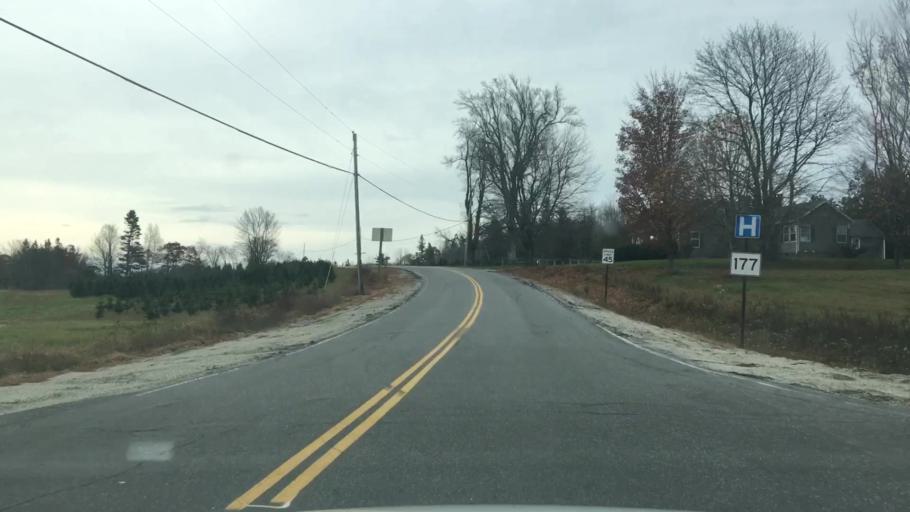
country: US
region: Maine
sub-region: Hancock County
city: Penobscot
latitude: 44.4429
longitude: -68.6365
